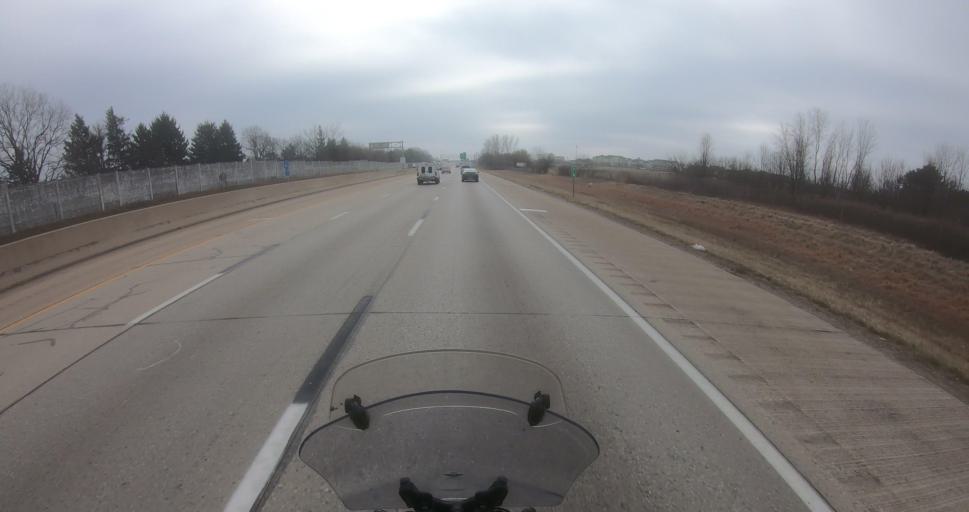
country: US
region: Ohio
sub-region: Miami County
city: Troy
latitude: 40.0659
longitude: -84.2334
